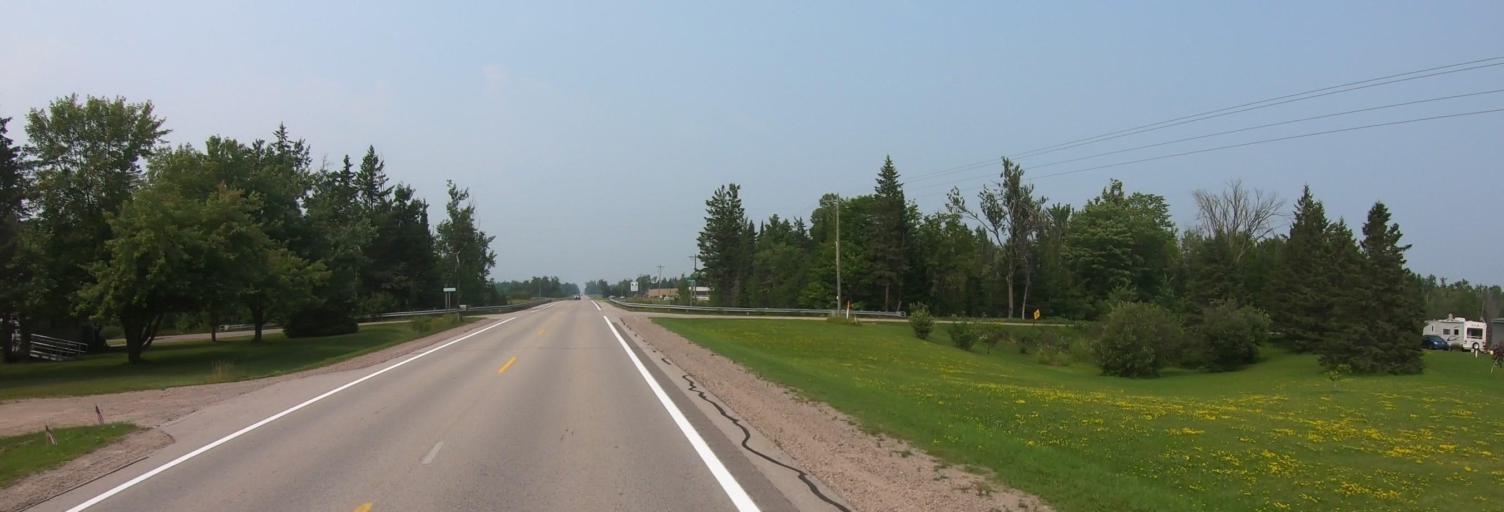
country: US
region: Michigan
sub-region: Chippewa County
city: Sault Ste. Marie
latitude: 46.2295
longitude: -84.3634
